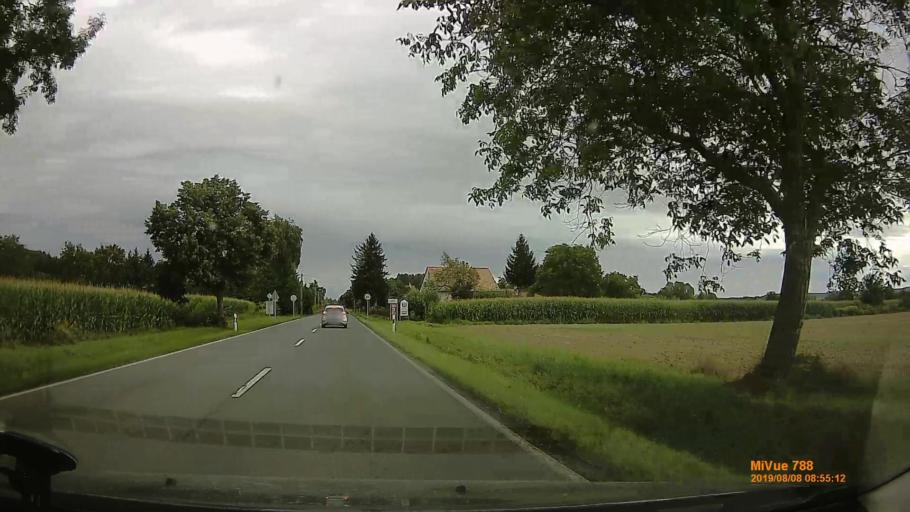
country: HU
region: Zala
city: Pacsa
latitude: 46.6236
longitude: 16.9203
